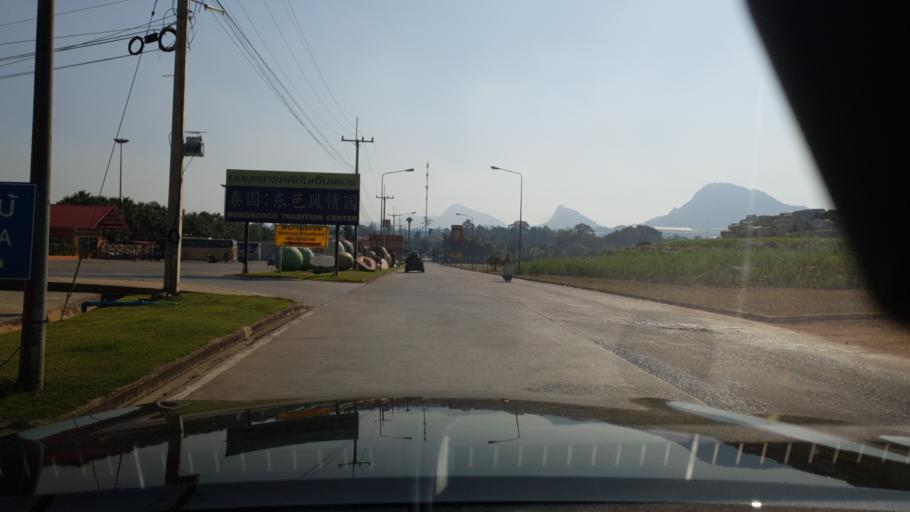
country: TH
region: Chon Buri
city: Sattahip
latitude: 12.7750
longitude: 100.9249
